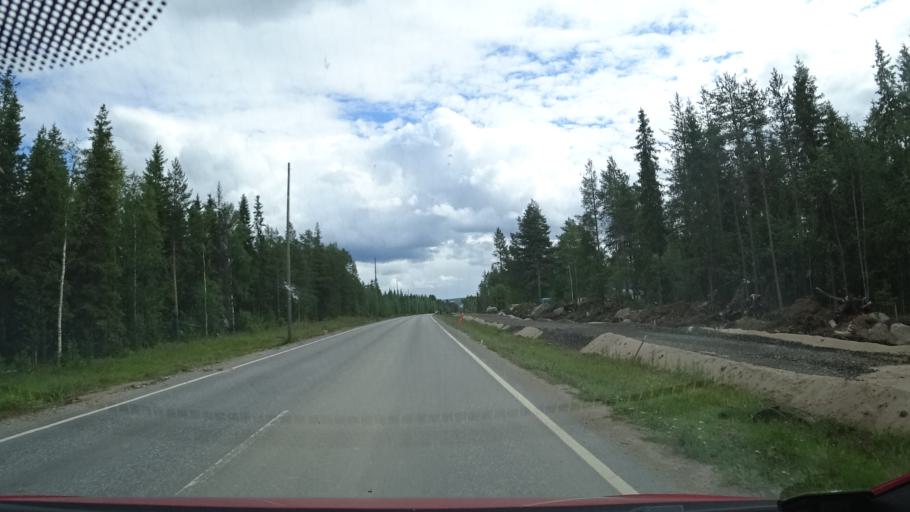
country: FI
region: Lapland
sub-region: Rovaniemi
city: Rovaniemi
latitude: 66.5372
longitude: 25.7250
